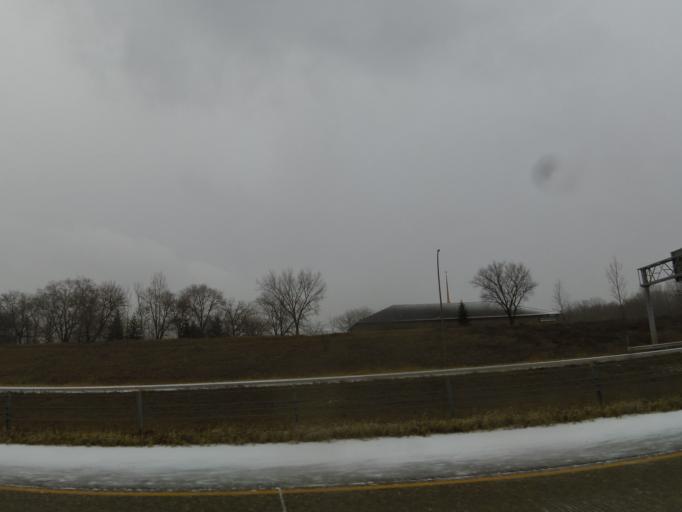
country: US
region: Minnesota
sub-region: Dakota County
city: Eagan
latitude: 44.8013
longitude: -93.2221
